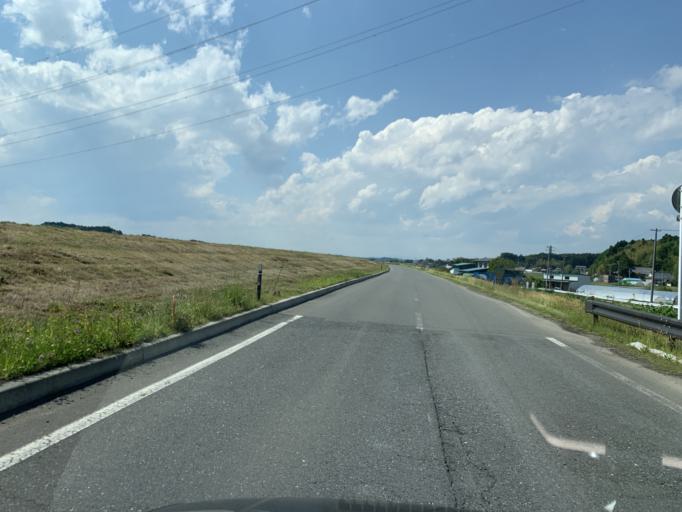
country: JP
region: Miyagi
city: Matsushima
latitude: 38.4301
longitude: 141.1242
